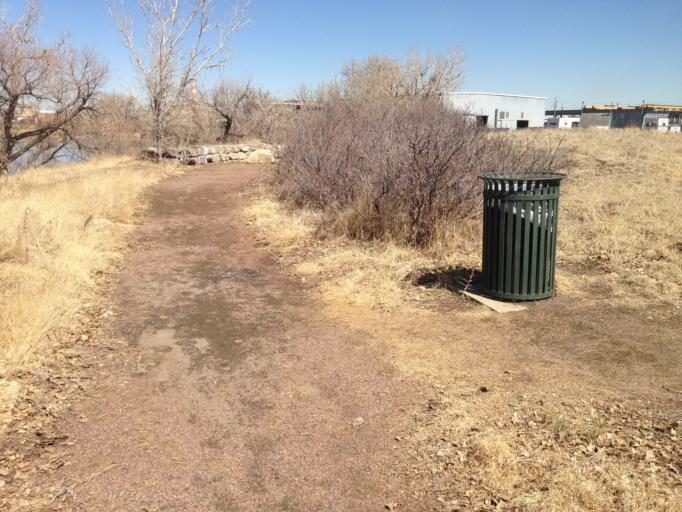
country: US
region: Colorado
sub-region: Adams County
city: Commerce City
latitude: 39.7927
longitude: -104.9722
